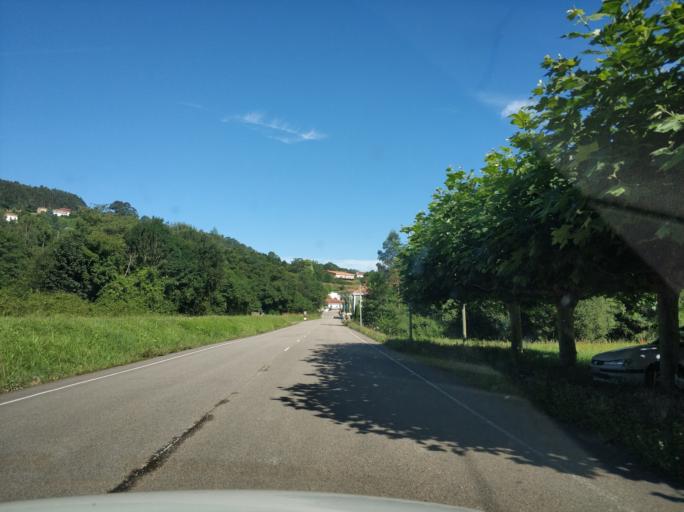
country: ES
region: Asturias
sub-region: Province of Asturias
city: Cudillero
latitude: 43.5584
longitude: -6.2283
